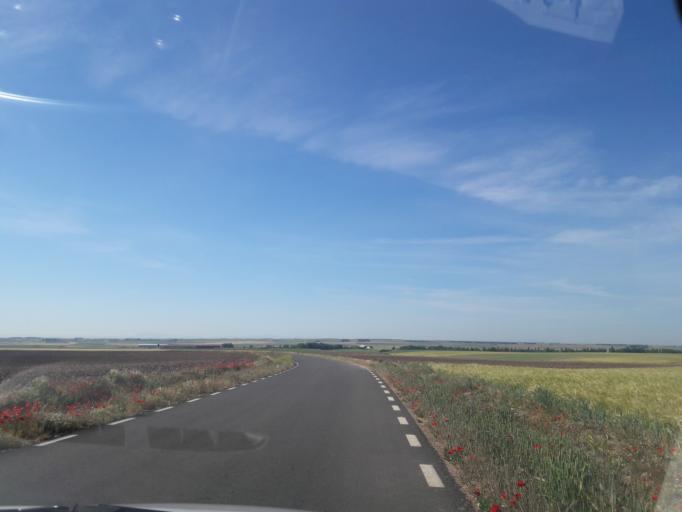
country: ES
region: Castille and Leon
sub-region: Provincia de Salamanca
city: Espino de la Orbada
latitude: 41.1222
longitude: -5.4289
